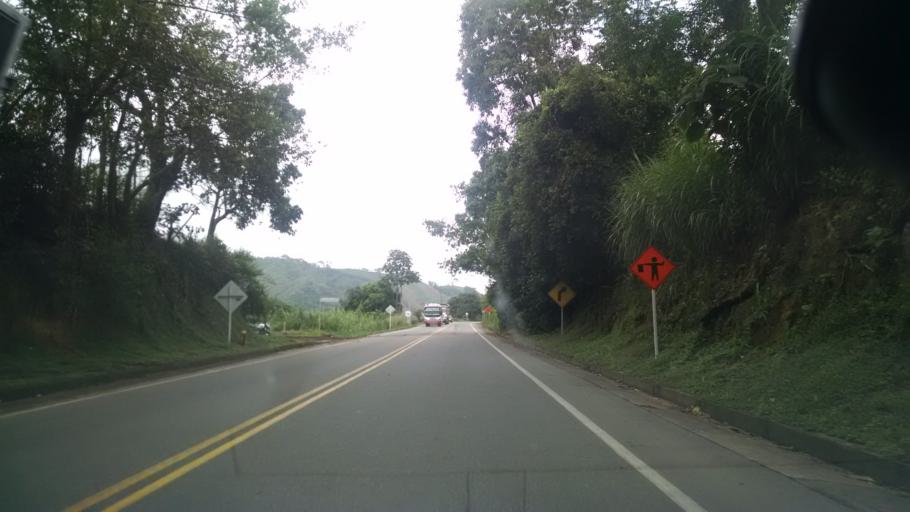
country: CO
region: Caldas
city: Palestina
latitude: 5.0689
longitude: -75.6362
